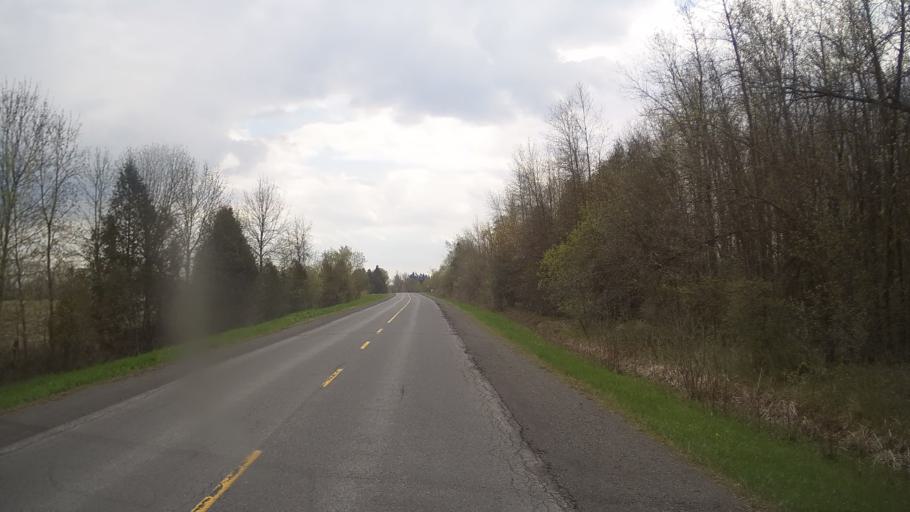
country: CA
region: Ontario
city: Hawkesbury
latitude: 45.5244
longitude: -74.5628
